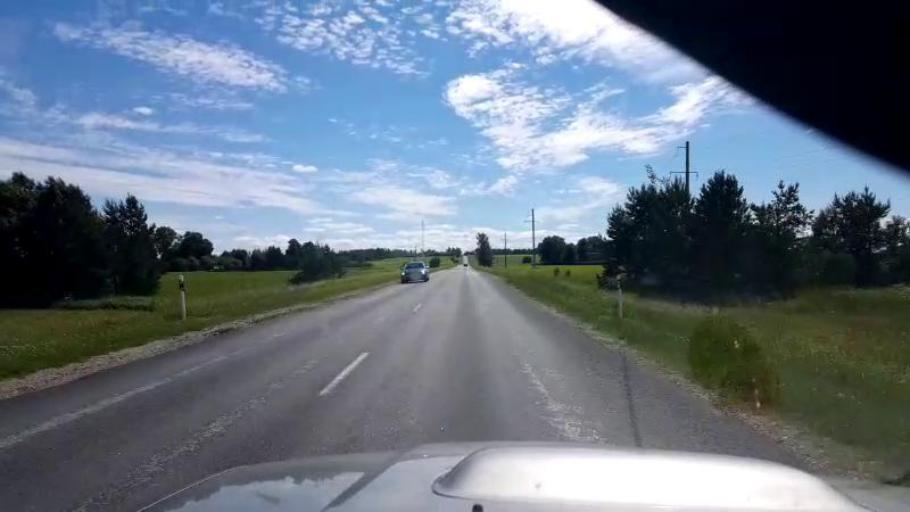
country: EE
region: Laeaene-Virumaa
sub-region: Rakke vald
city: Rakke
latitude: 58.8623
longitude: 26.2936
